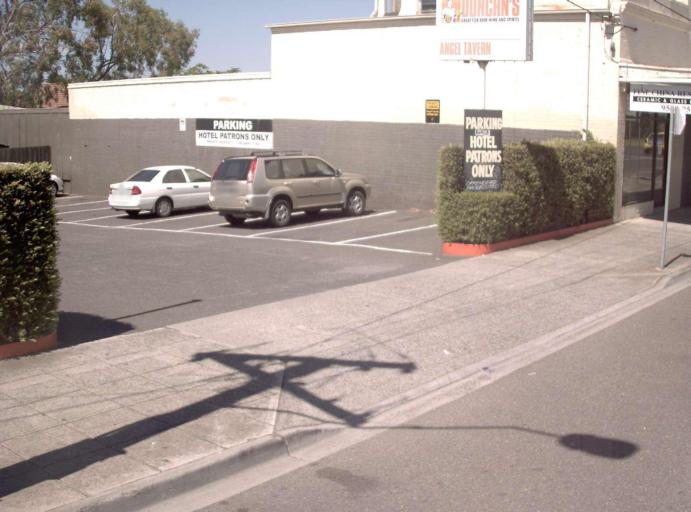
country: AU
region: Victoria
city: Caulfield North
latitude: -37.8663
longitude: 145.0282
